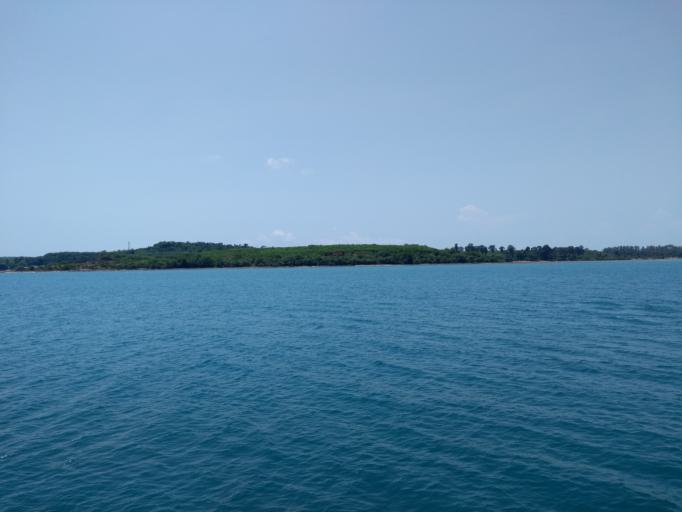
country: TH
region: Trat
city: Ko Kut
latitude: 11.8085
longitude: 102.5102
